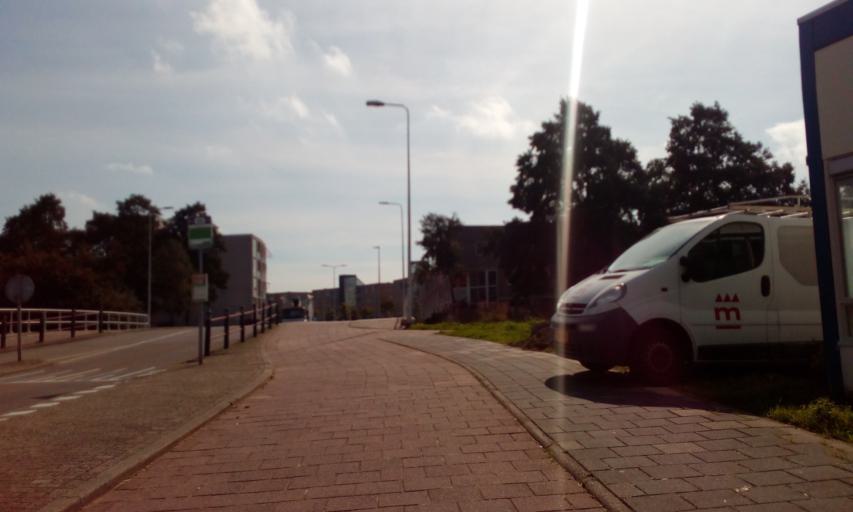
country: NL
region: South Holland
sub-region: Gemeente Voorschoten
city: Voorschoten
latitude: 52.1475
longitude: 4.4498
